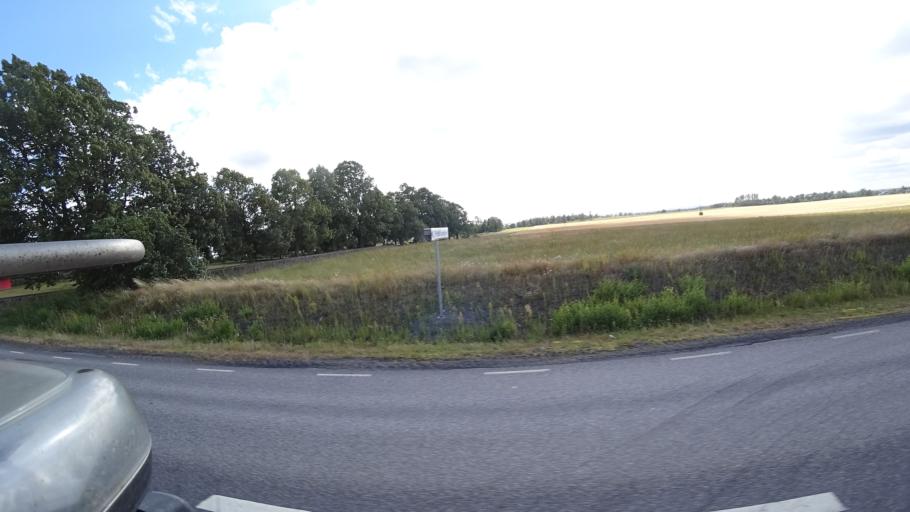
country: SE
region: Skane
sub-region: Kristianstads Kommun
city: Onnestad
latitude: 56.0756
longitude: 14.0840
